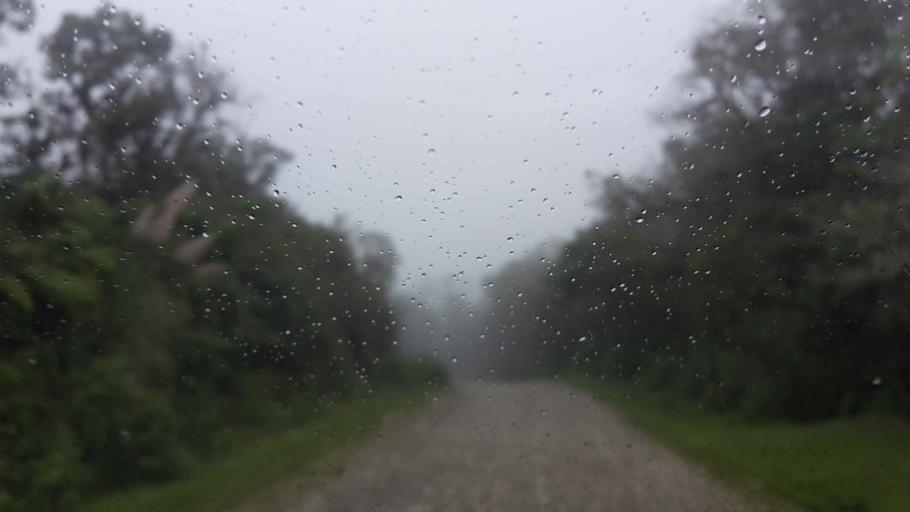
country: BO
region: Cochabamba
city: Colomi
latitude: -17.1257
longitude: -65.9647
